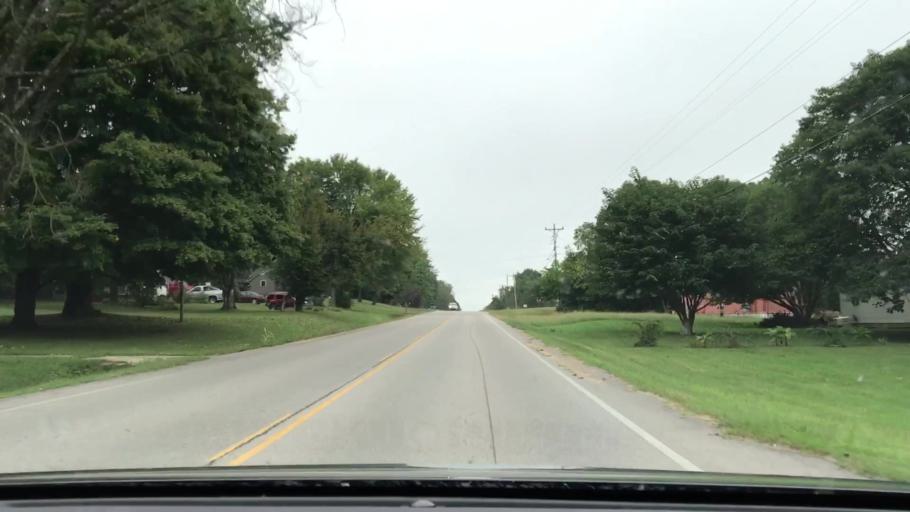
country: US
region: Tennessee
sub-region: Sumner County
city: Portland
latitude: 36.5064
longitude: -86.4991
